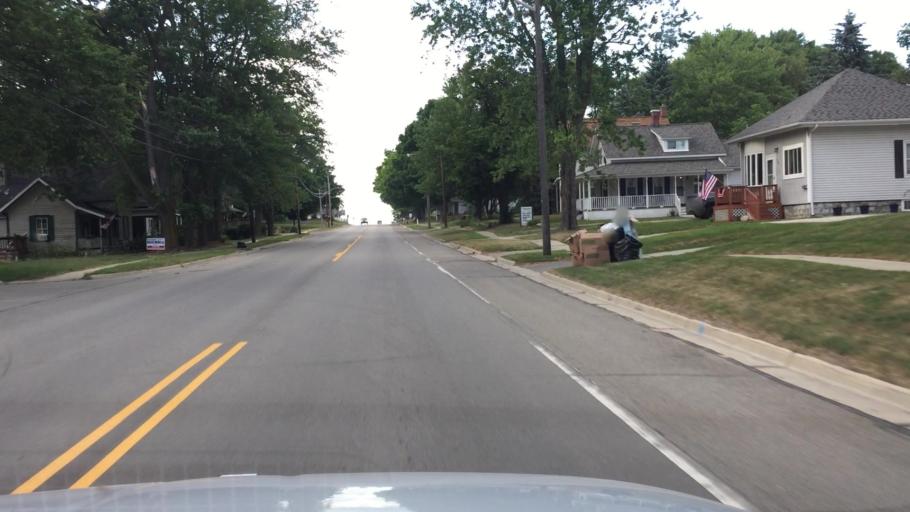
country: US
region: Michigan
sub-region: Saint Clair County
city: Yale
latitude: 43.1350
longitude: -82.7986
